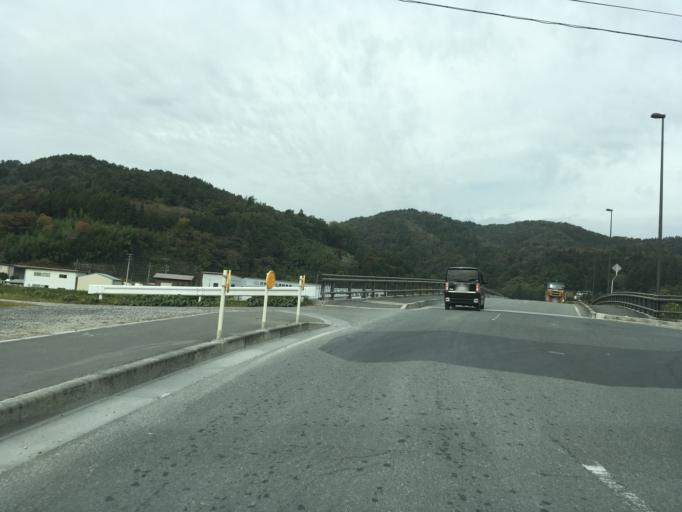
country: JP
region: Iwate
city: Ichinoseki
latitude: 38.9763
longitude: 141.2411
